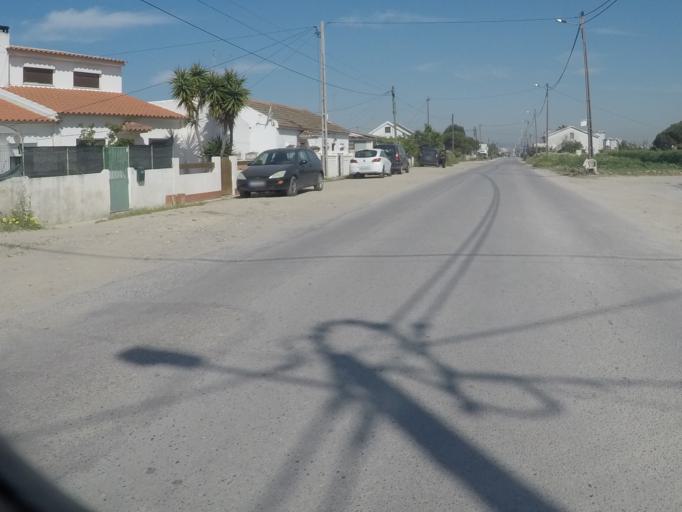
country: PT
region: Setubal
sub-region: Almada
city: Costa de Caparica
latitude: 38.6293
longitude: -9.2212
